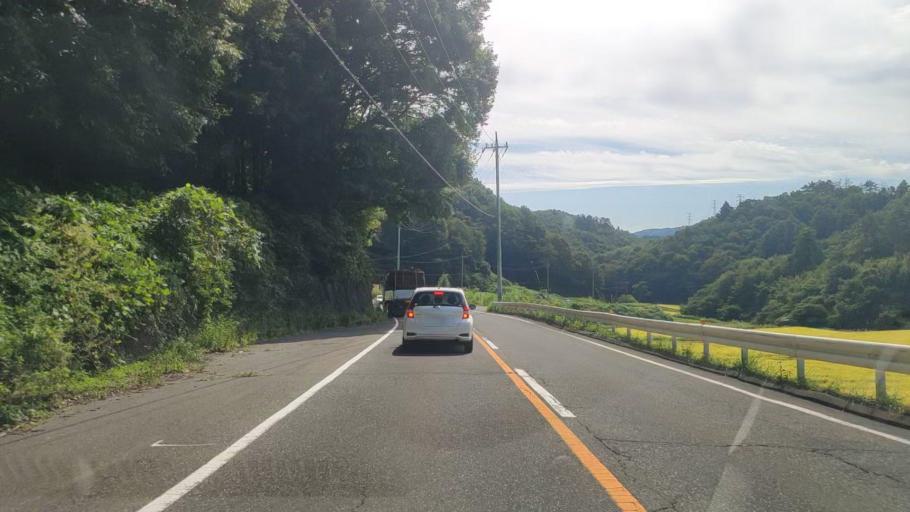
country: JP
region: Gunma
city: Numata
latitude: 36.6310
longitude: 138.9954
